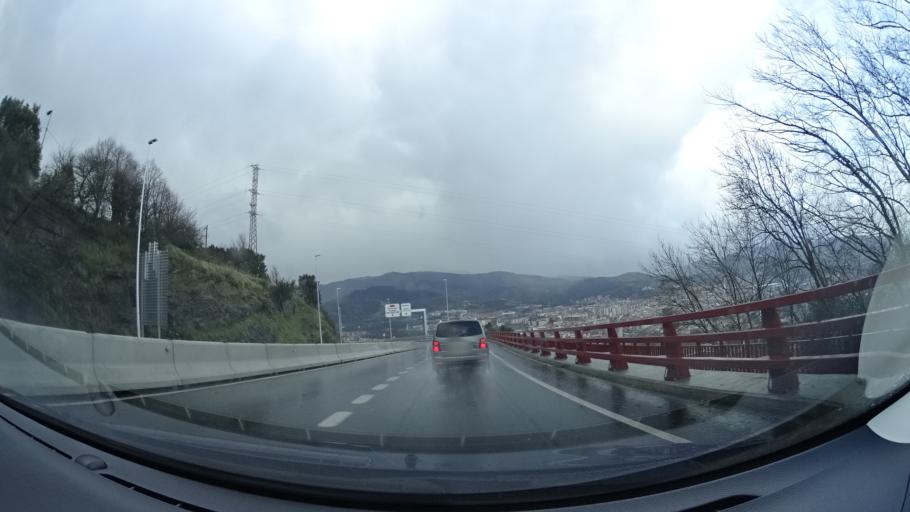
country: ES
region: Basque Country
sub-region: Bizkaia
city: Santutxu
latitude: 43.2665
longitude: -2.9074
